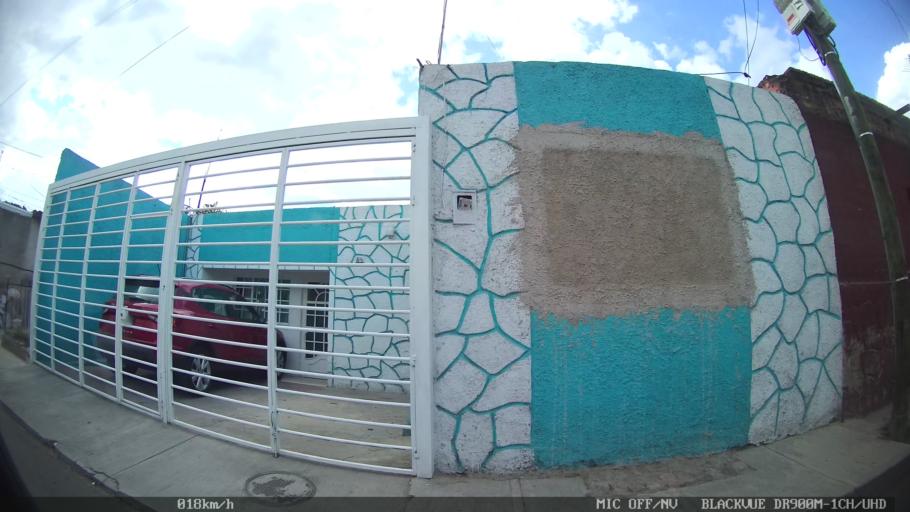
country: MX
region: Jalisco
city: Tlaquepaque
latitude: 20.6590
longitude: -103.2611
